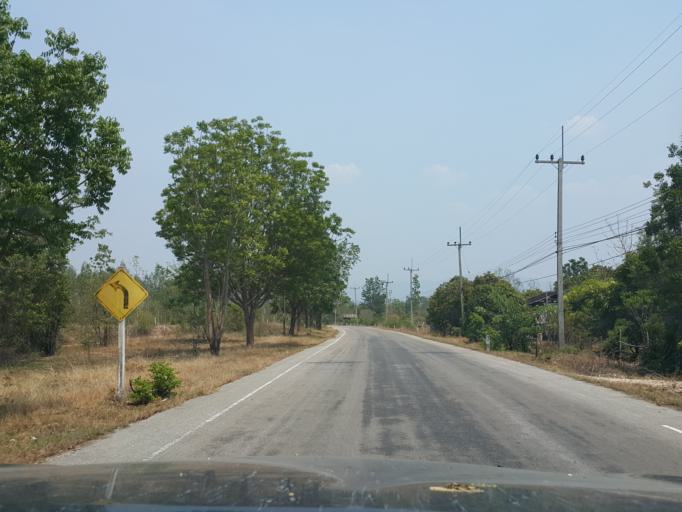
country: TH
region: Lampang
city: Mae Phrik
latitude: 17.5379
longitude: 99.1419
